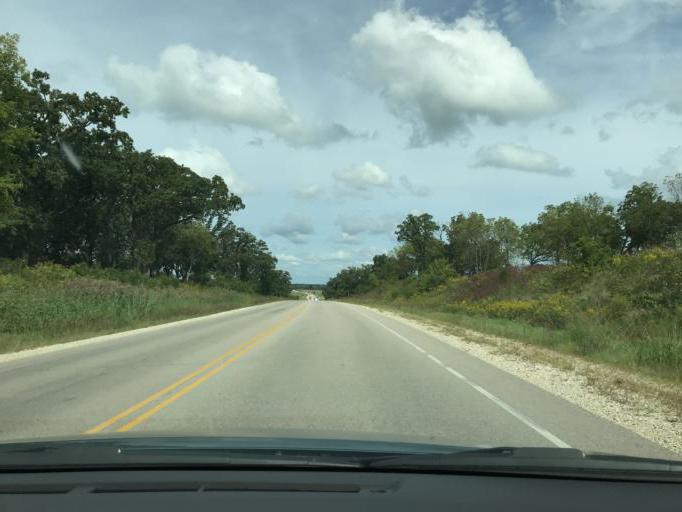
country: US
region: Wisconsin
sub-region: Racine County
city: Bohners Lake
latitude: 42.6035
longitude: -88.2241
